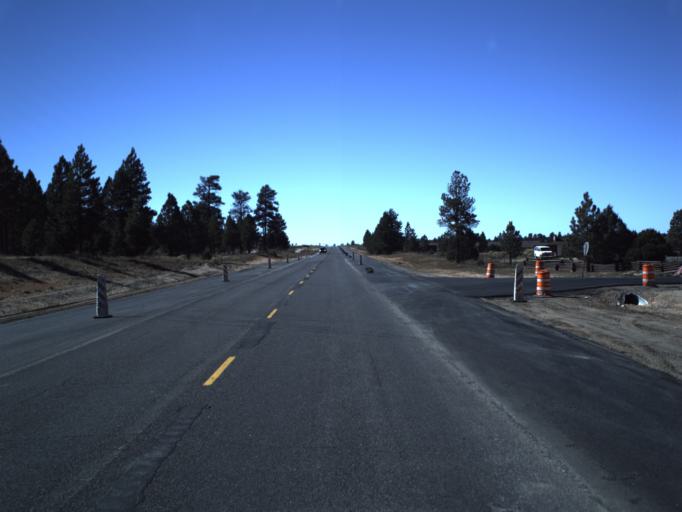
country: US
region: Utah
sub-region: Garfield County
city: Panguitch
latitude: 37.7100
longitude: -112.2116
